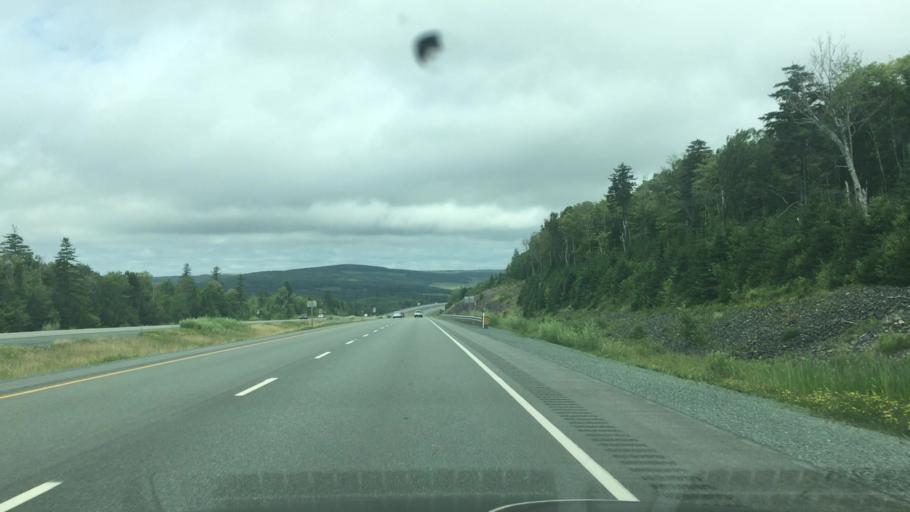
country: CA
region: Nova Scotia
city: Oxford
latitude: 45.5213
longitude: -63.7022
